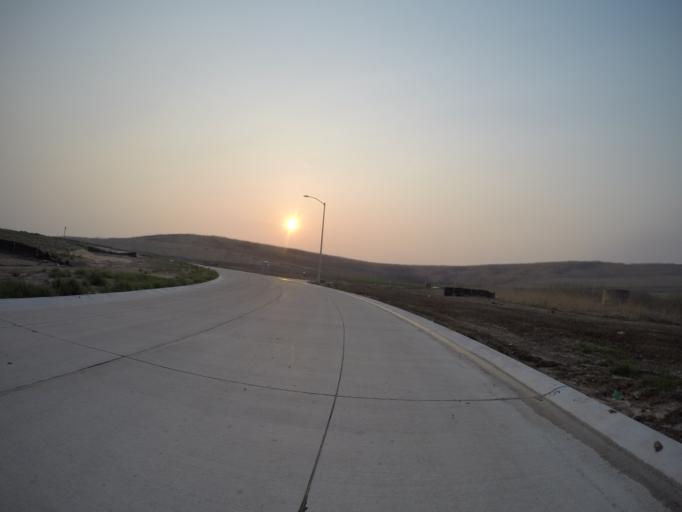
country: US
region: Kansas
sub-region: Riley County
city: Manhattan
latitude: 39.2213
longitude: -96.6436
